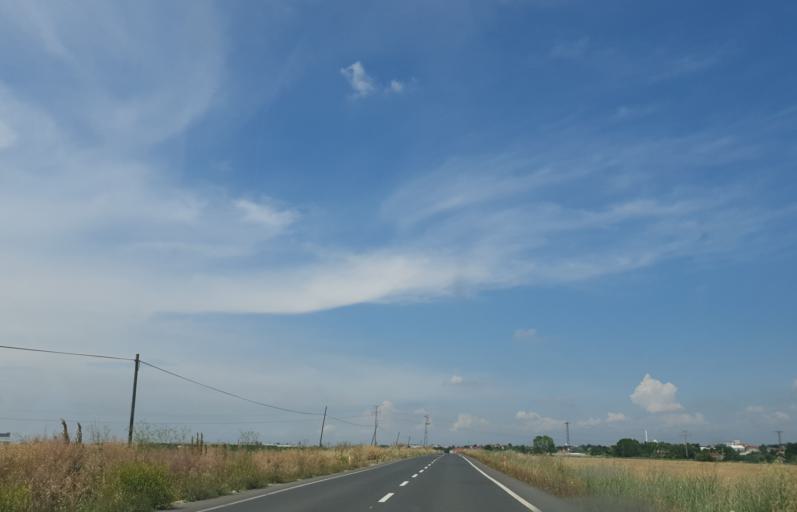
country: TR
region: Kirklareli
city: Buyukkaristiran
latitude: 41.2550
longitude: 27.6281
